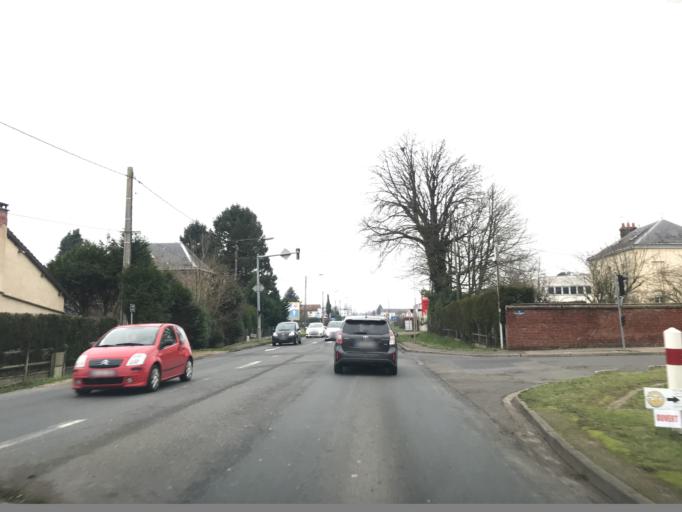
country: FR
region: Haute-Normandie
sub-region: Departement de la Seine-Maritime
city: Boos
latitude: 49.3955
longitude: 1.1841
